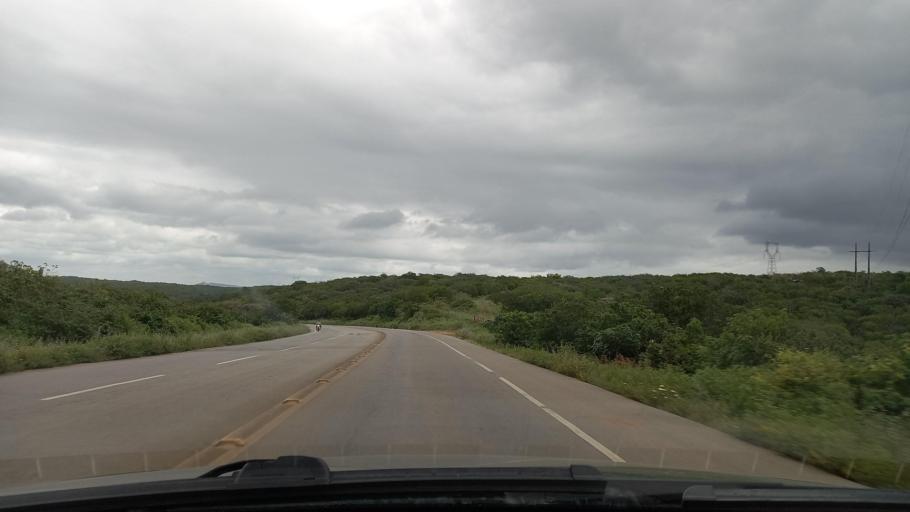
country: BR
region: Sergipe
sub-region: Caninde De Sao Francisco
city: Caninde de Sao Francisco
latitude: -9.6511
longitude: -37.7912
